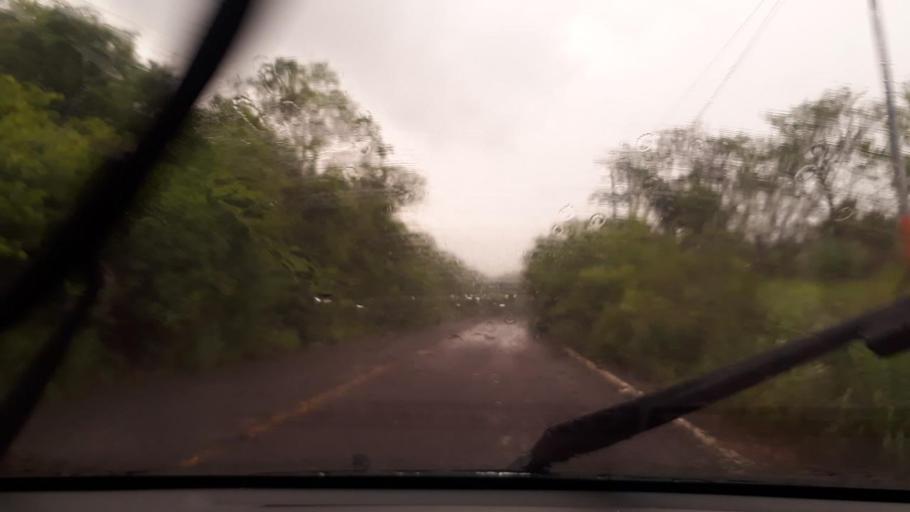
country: GT
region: Jutiapa
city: Comapa
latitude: 14.0718
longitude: -89.9542
